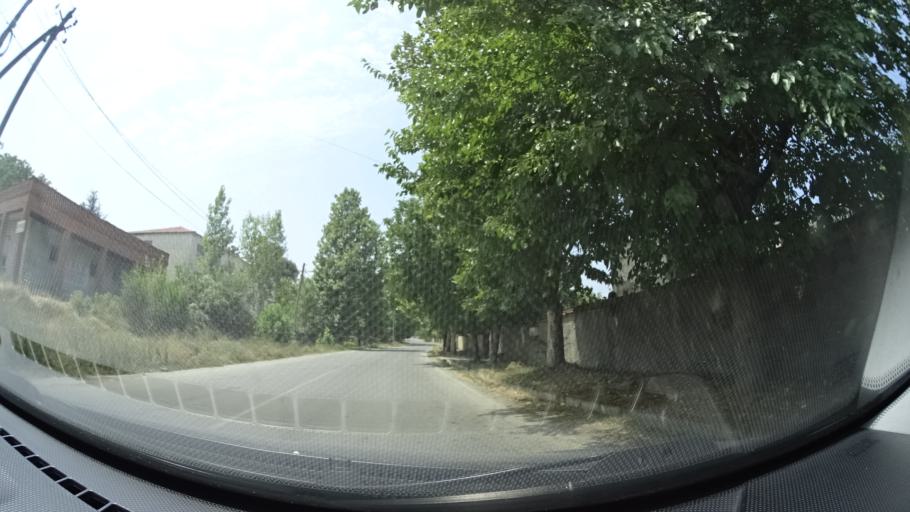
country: GE
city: Tsnori
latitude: 41.6212
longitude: 45.9680
